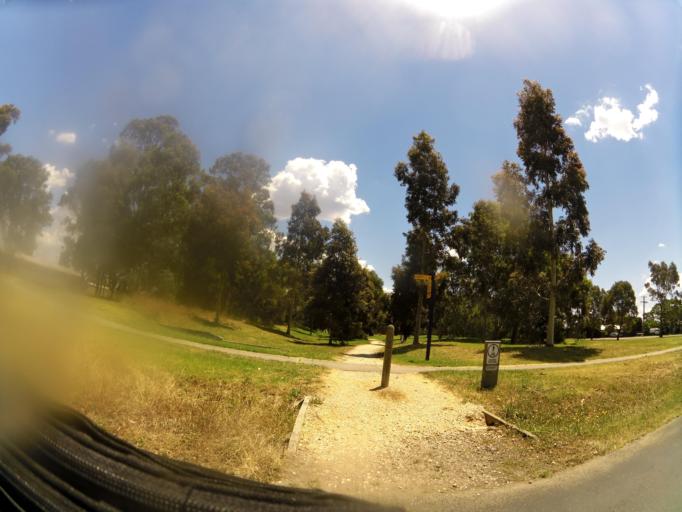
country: AU
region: Victoria
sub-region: Wellington
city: Heyfield
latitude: -37.9799
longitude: 146.7905
